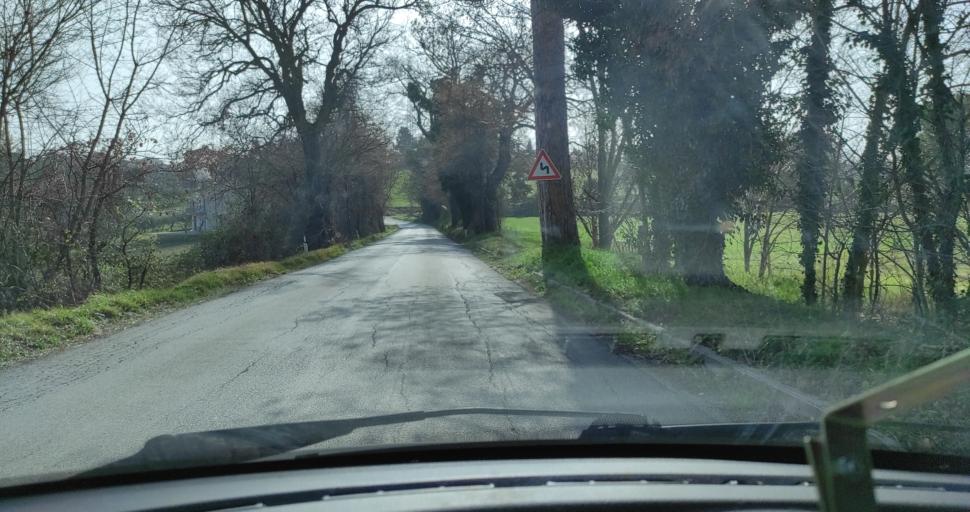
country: IT
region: The Marches
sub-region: Provincia di Macerata
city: Loro Piceno
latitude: 43.1680
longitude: 13.4027
